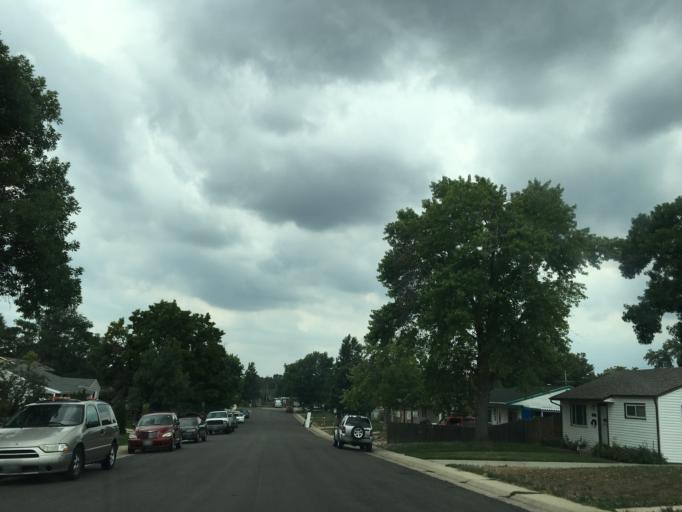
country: US
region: Colorado
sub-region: Arapahoe County
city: Sheridan
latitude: 39.6840
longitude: -105.0139
